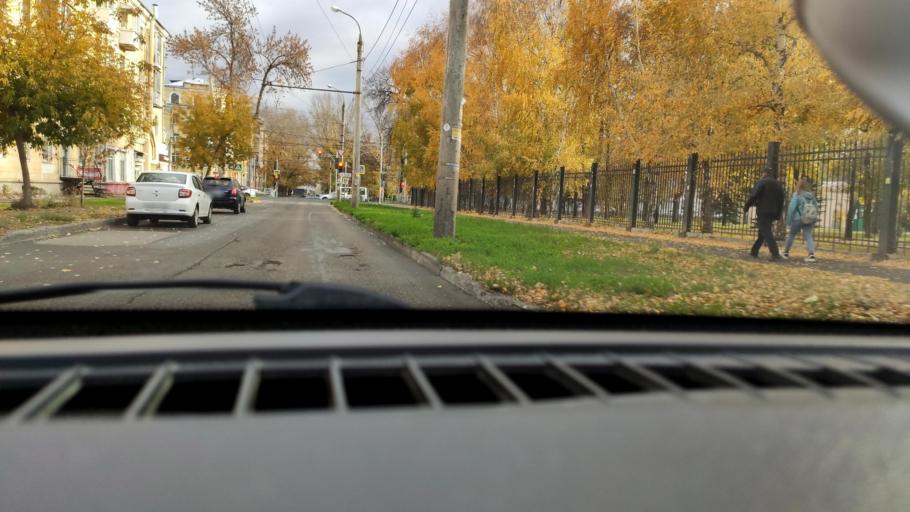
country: RU
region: Samara
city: Samara
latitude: 53.2168
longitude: 50.2549
